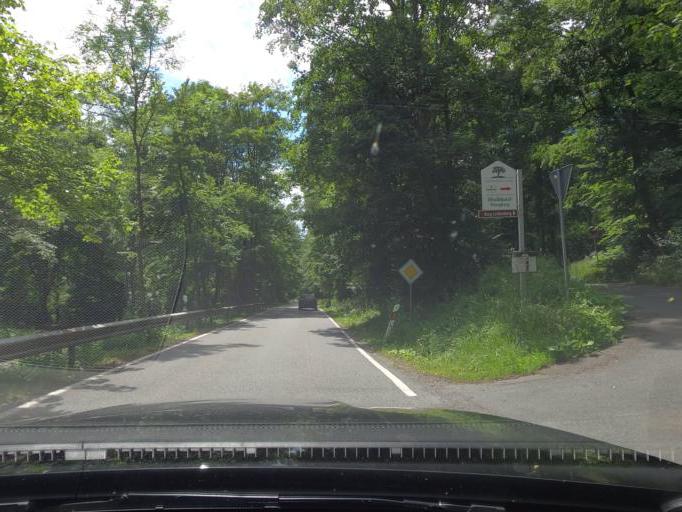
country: DE
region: Lower Saxony
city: Elbe
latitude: 52.1207
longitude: 10.2916
